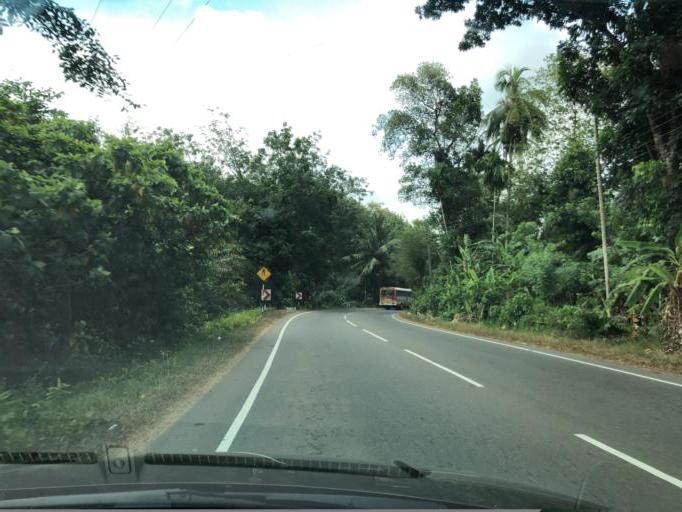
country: LK
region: Western
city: Horana South
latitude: 6.6284
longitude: 80.0776
